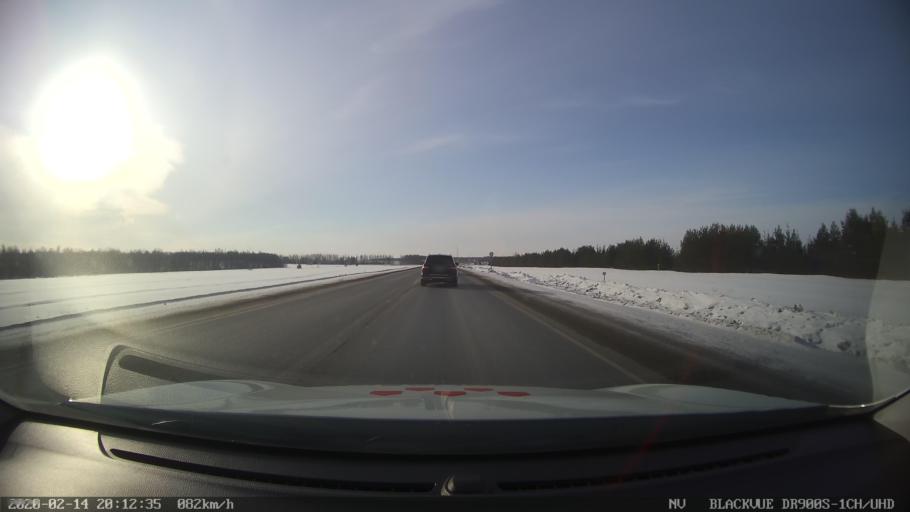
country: RU
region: Tatarstan
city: Verkhniy Uslon
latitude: 55.6641
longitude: 48.8612
